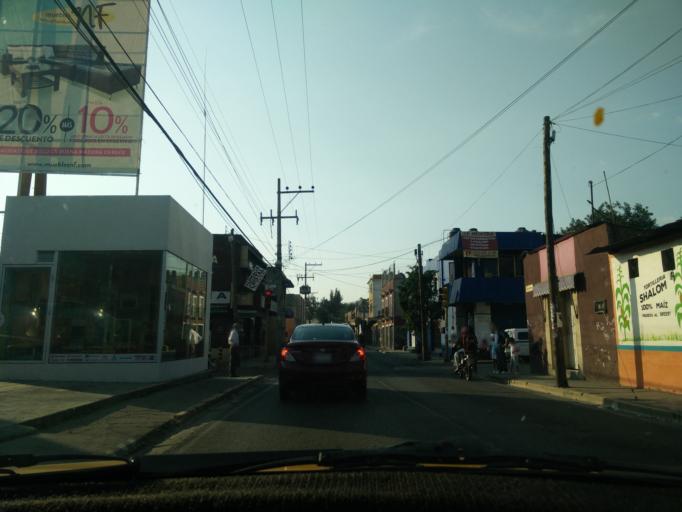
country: MX
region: Oaxaca
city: Oaxaca de Juarez
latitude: 17.0737
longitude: -96.7381
